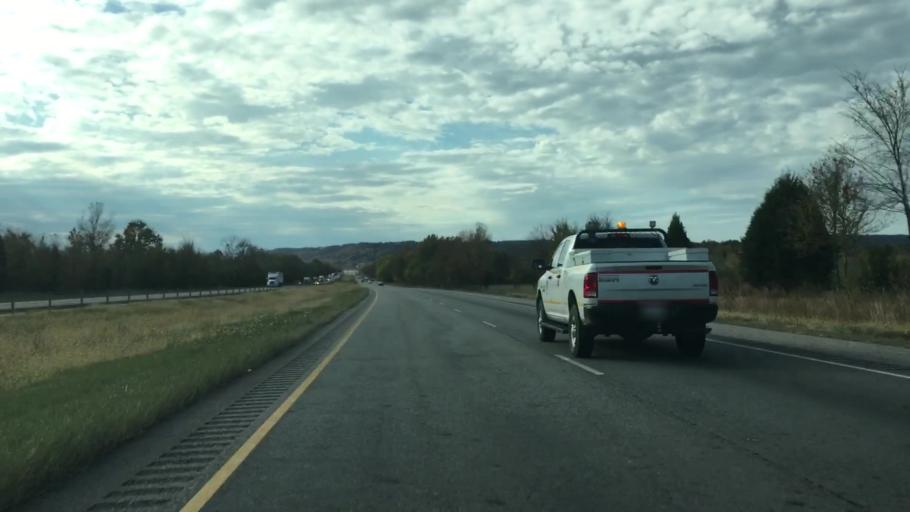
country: US
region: Arkansas
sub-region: Pope County
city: Atkins
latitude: 35.2517
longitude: -92.8947
